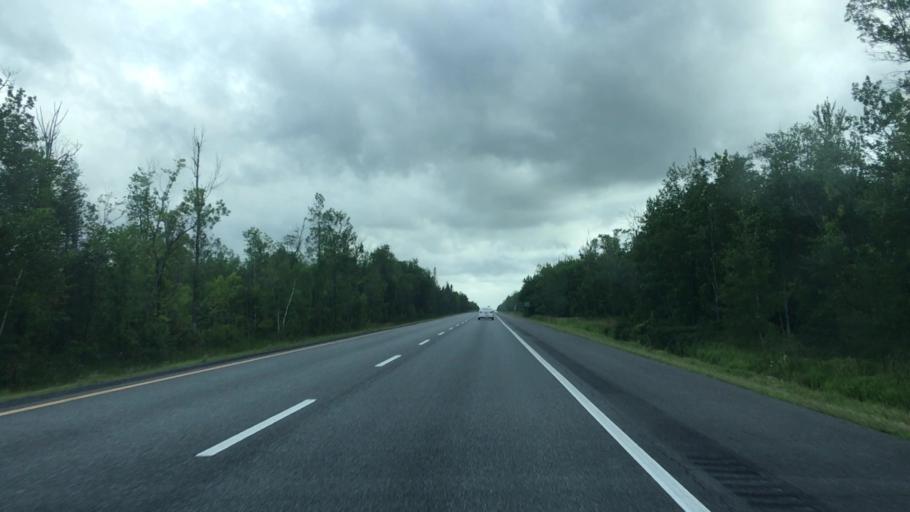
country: US
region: Maine
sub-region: Waldo County
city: Burnham
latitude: 44.6862
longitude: -69.4749
